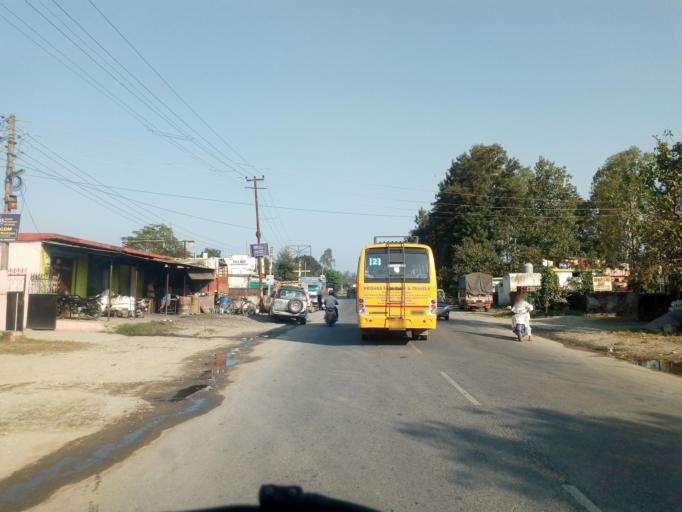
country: IN
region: Uttarakhand
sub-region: Dehradun
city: Dehradun
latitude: 30.3446
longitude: 77.9109
